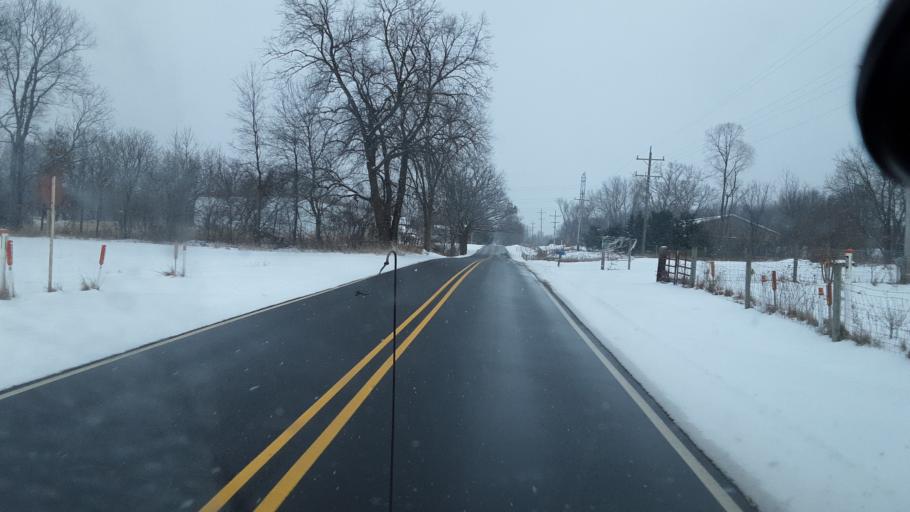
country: US
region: Michigan
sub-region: Ingham County
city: Leslie
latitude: 42.4194
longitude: -84.4433
